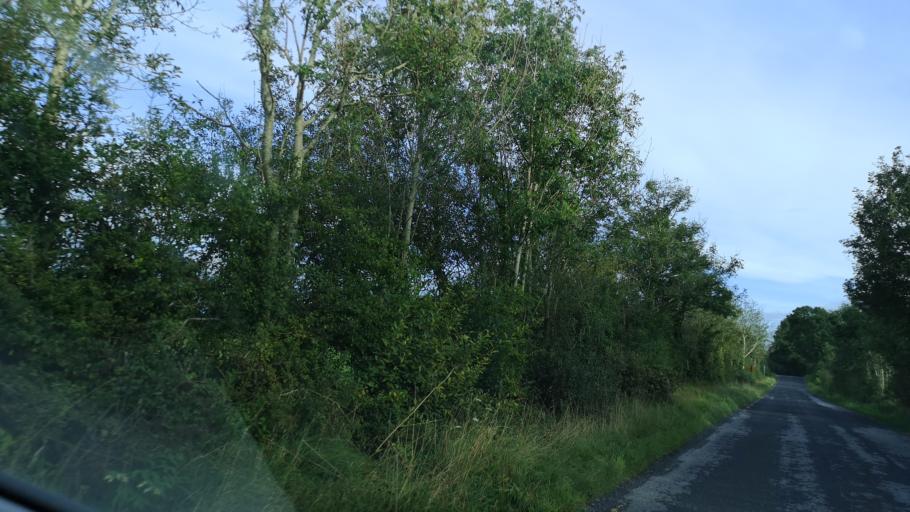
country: IE
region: Connaught
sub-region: County Galway
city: Ballinasloe
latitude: 53.3391
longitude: -8.2906
